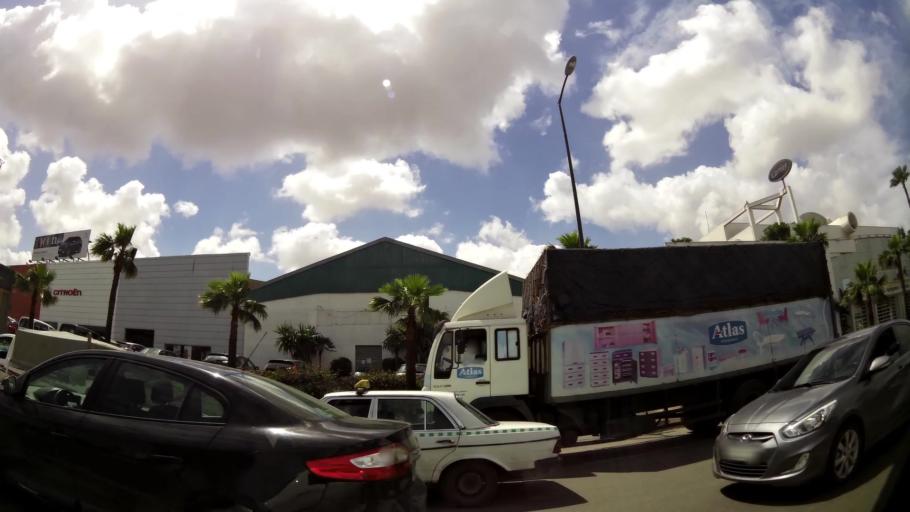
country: MA
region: Grand Casablanca
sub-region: Mediouna
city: Tit Mellil
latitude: 33.6020
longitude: -7.5211
